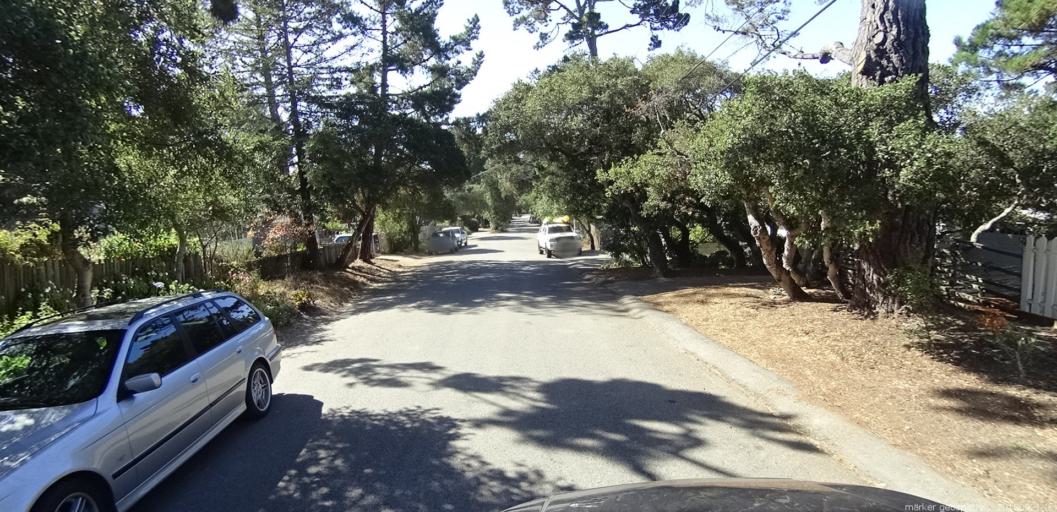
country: US
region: California
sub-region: Monterey County
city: Carmel-by-the-Sea
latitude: 36.5615
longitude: -121.9140
